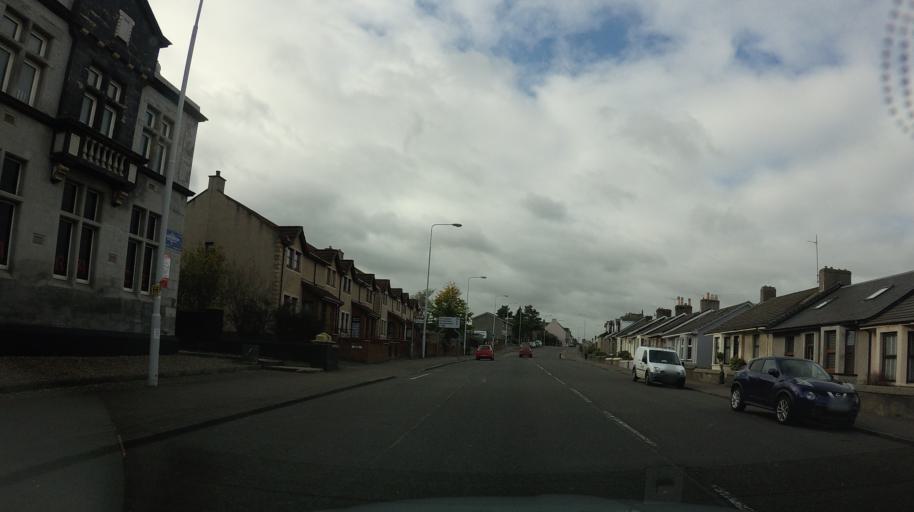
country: GB
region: Scotland
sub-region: Fife
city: Cowdenbeath
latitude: 56.1073
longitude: -3.3438
